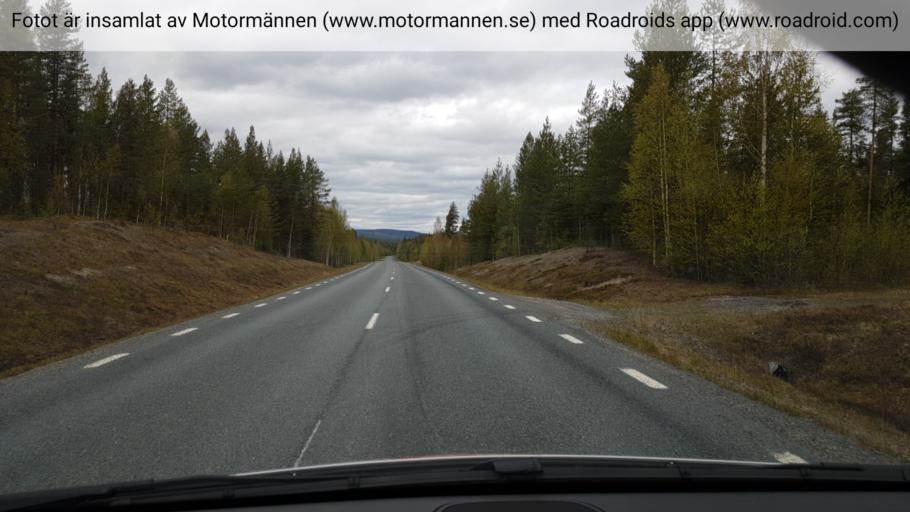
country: SE
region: Vaesterbotten
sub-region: Mala Kommun
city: Mala
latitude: 65.0678
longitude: 18.3658
